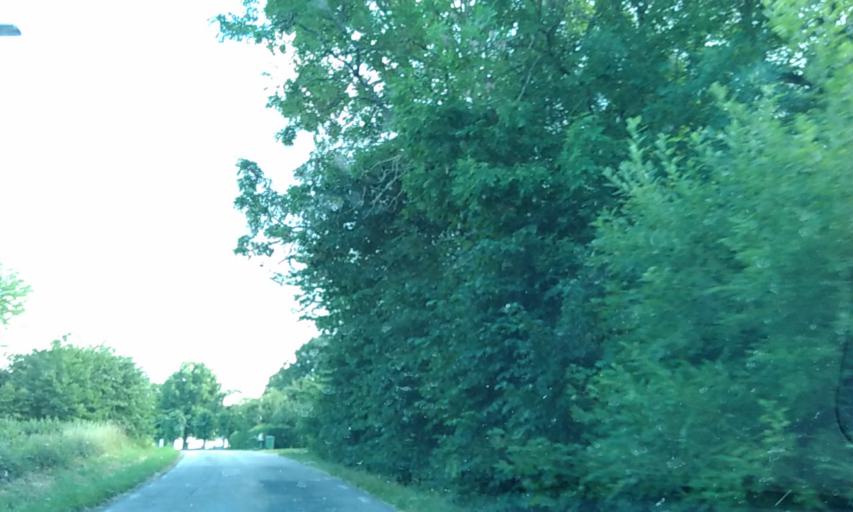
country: SE
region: Vaestra Goetaland
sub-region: Lidkopings Kommun
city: Lidkoping
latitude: 58.5521
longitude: 13.0079
